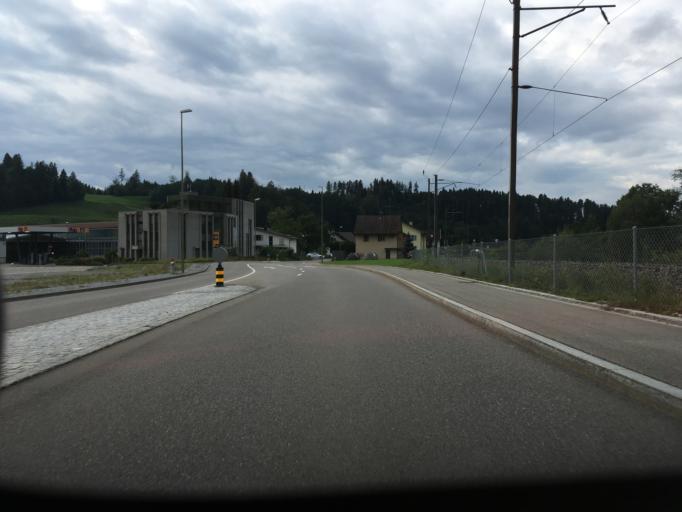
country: CH
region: Zurich
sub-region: Bezirk Pfaeffikon
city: Bauma
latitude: 47.3797
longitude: 8.8611
